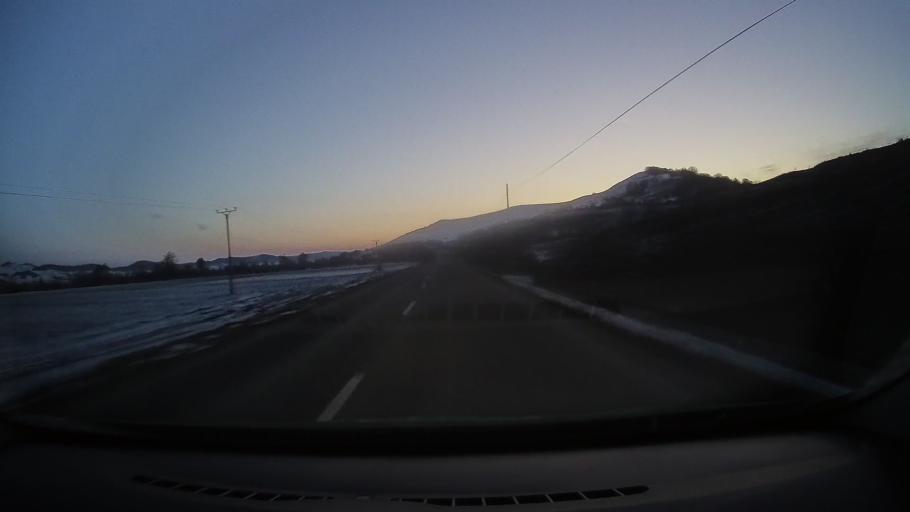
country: RO
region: Sibiu
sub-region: Comuna Alma
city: Alma
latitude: 46.2023
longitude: 24.4506
